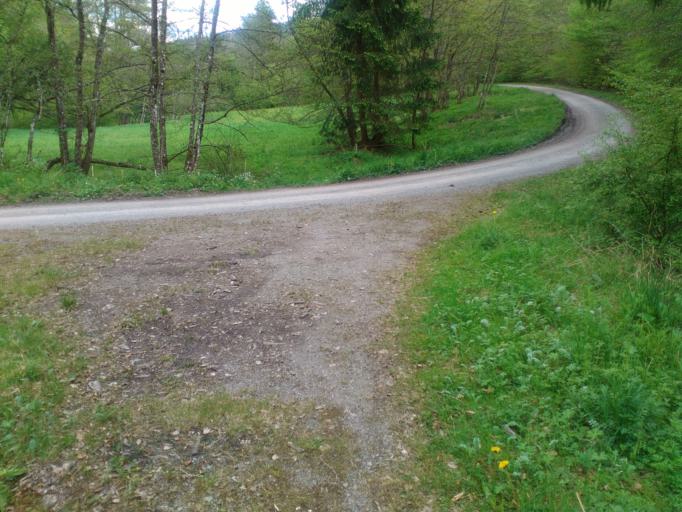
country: DE
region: Baden-Wuerttemberg
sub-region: Tuebingen Region
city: Dettenhausen
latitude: 48.6000
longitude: 9.1197
